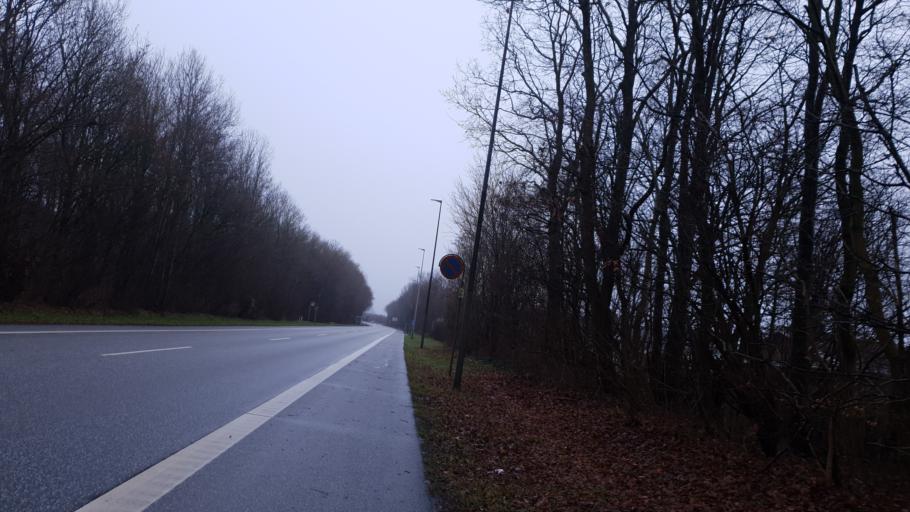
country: DK
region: Central Jutland
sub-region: Hedensted Kommune
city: Hedensted
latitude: 55.7851
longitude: 9.6988
